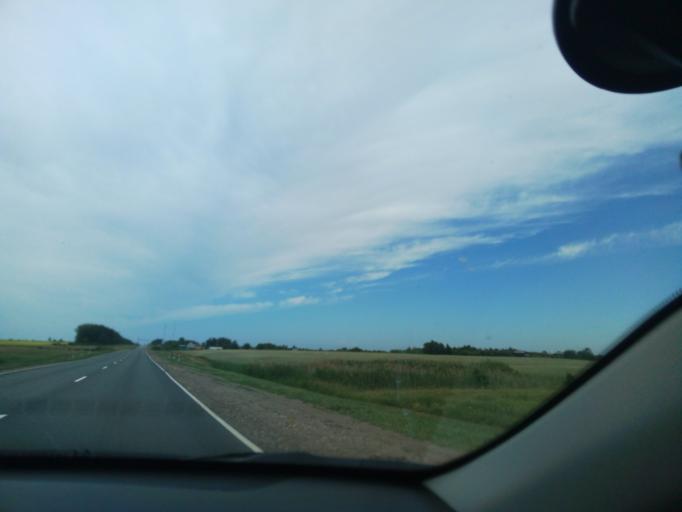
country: RU
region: Tambov
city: Selezni
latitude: 52.6317
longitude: 40.9077
